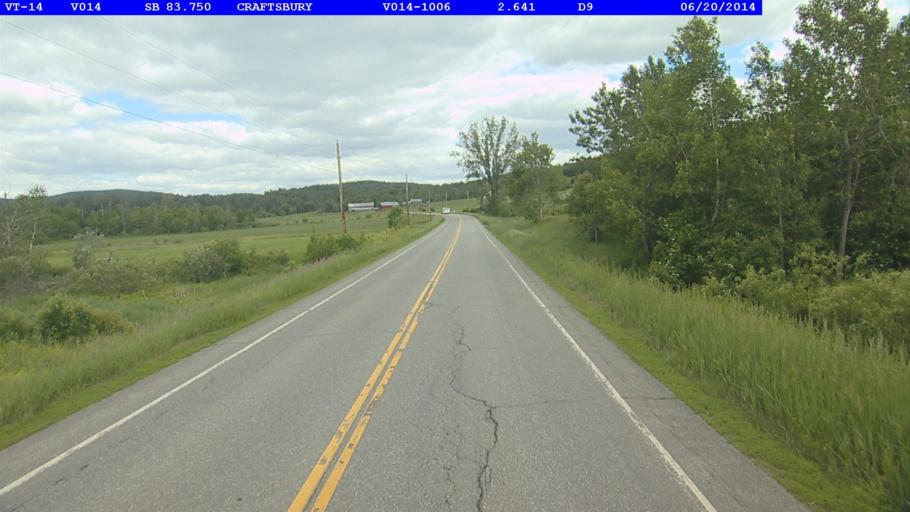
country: US
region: Vermont
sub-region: Caledonia County
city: Hardwick
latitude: 44.6312
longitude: -72.3921
